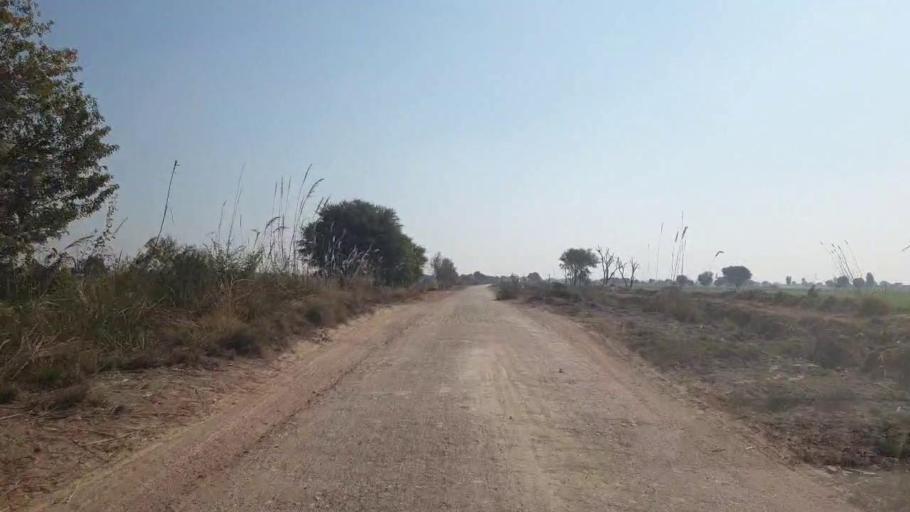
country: PK
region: Sindh
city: Shahdadpur
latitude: 25.9557
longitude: 68.6274
